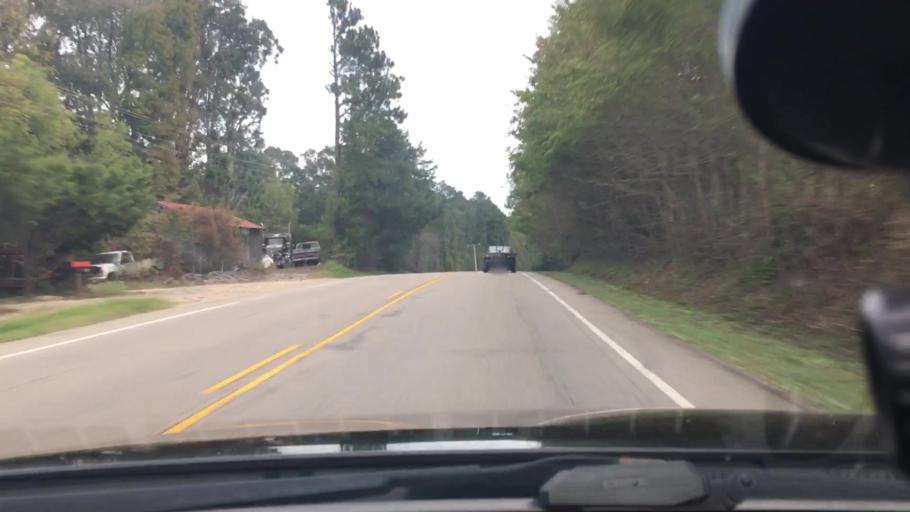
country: US
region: North Carolina
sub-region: Moore County
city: Robbins
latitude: 35.3982
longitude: -79.5401
